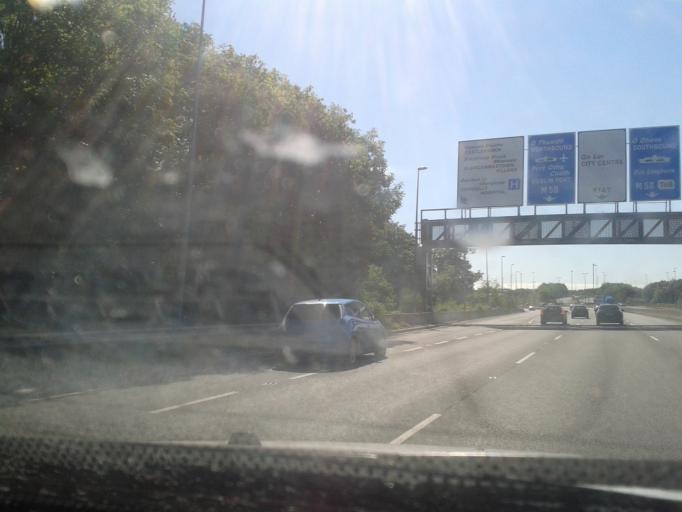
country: IE
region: Leinster
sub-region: Fingal County
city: Blanchardstown
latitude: 53.3872
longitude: -6.3723
